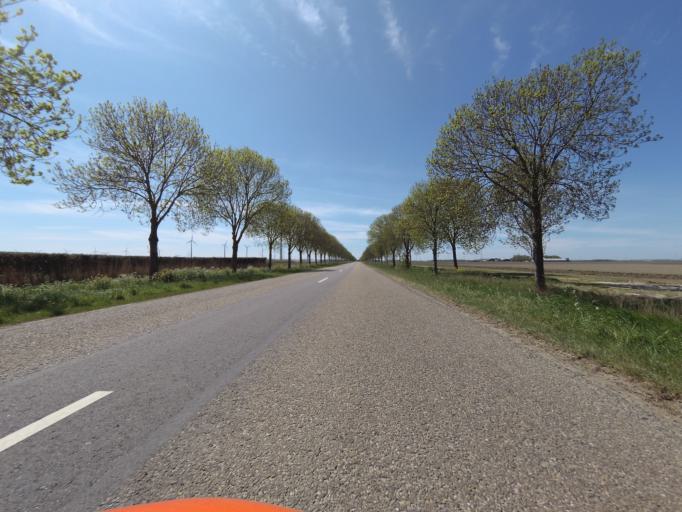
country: NL
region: Flevoland
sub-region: Gemeente Zeewolde
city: Zeewolde
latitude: 52.3483
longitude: 5.4484
